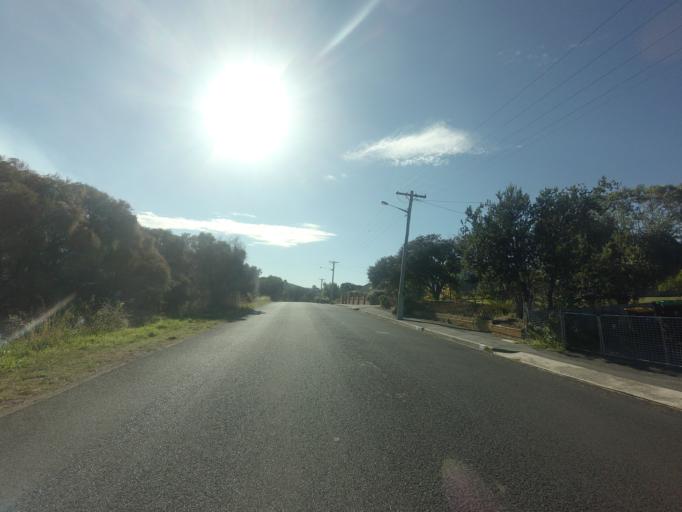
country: AU
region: Tasmania
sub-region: Clarence
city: Bellerive
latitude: -42.8690
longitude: 147.3539
